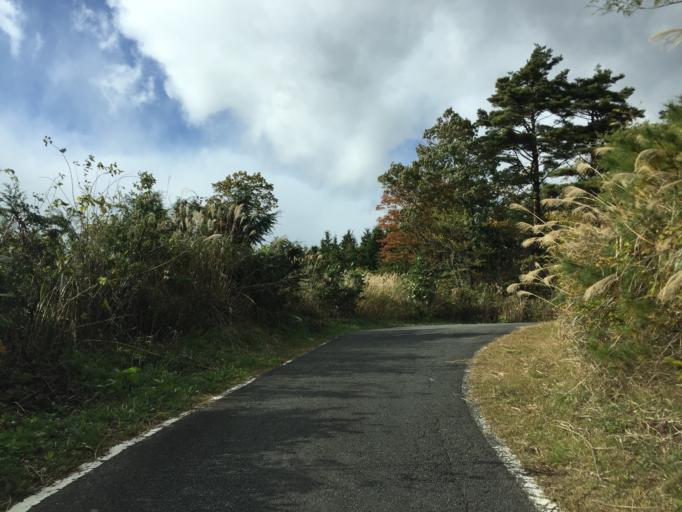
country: JP
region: Fukushima
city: Nihommatsu
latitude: 37.6793
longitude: 140.3712
